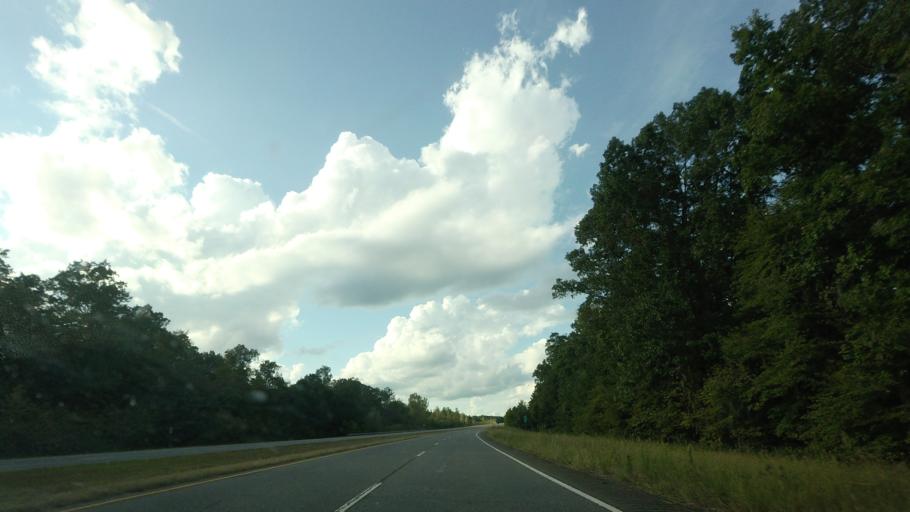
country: US
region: Georgia
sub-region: Houston County
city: Perry
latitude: 32.3985
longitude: -83.6414
